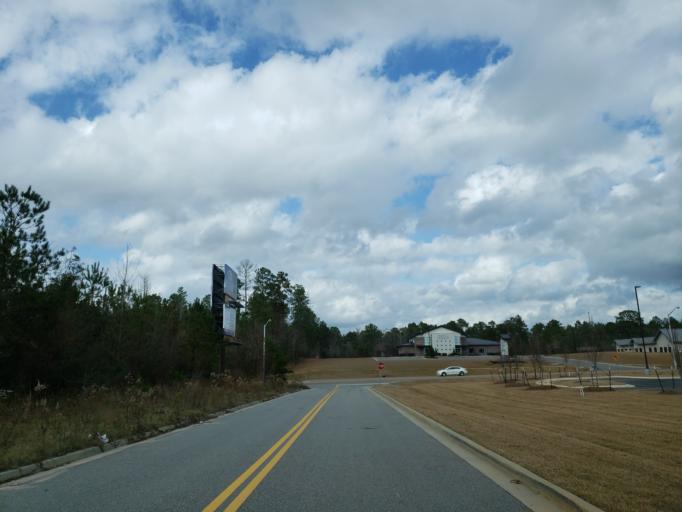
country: US
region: Mississippi
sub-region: Lamar County
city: West Hattiesburg
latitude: 31.3005
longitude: -89.3646
